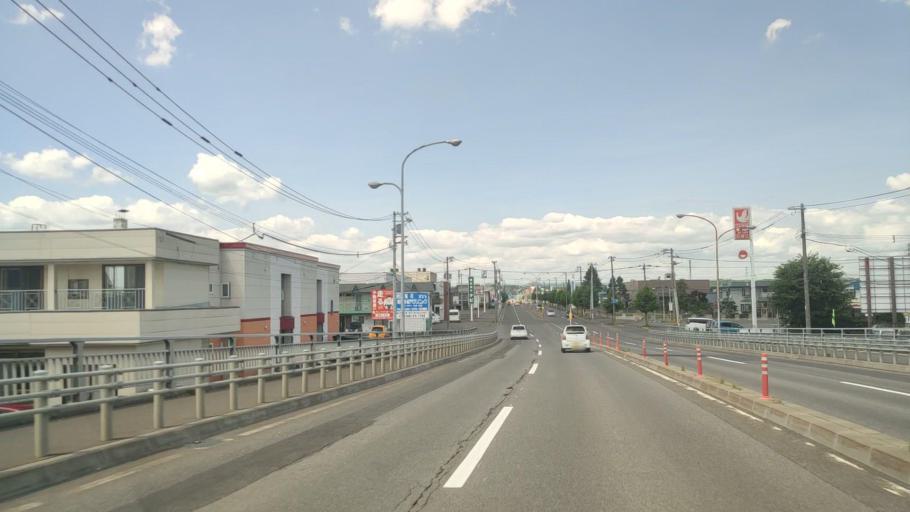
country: JP
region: Hokkaido
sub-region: Asahikawa-shi
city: Asahikawa
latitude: 43.7992
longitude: 142.3944
